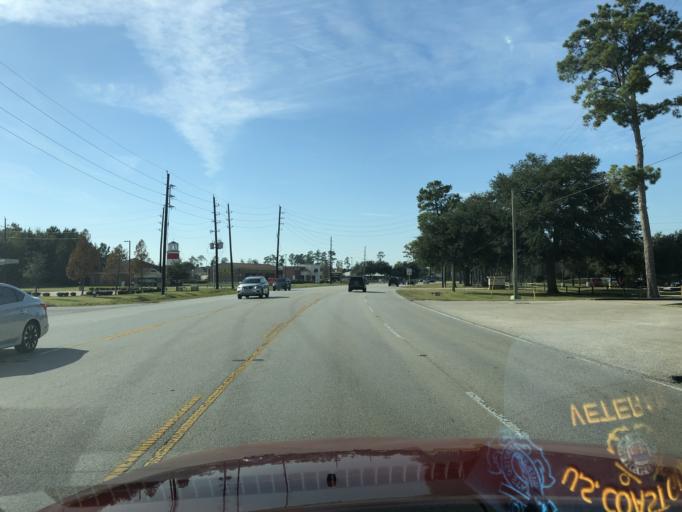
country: US
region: Texas
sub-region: Harris County
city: Tomball
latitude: 30.0314
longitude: -95.5566
